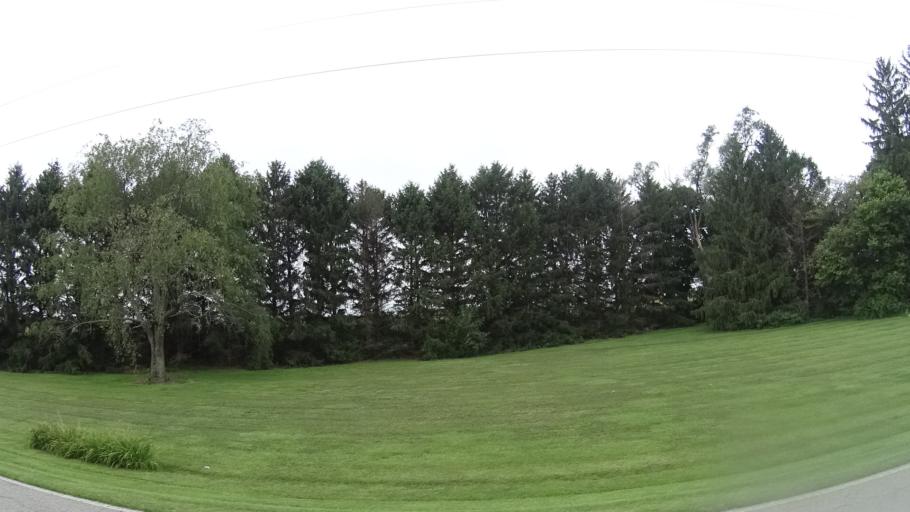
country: US
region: Indiana
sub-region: Madison County
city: Lapel
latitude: 40.0582
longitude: -85.8346
